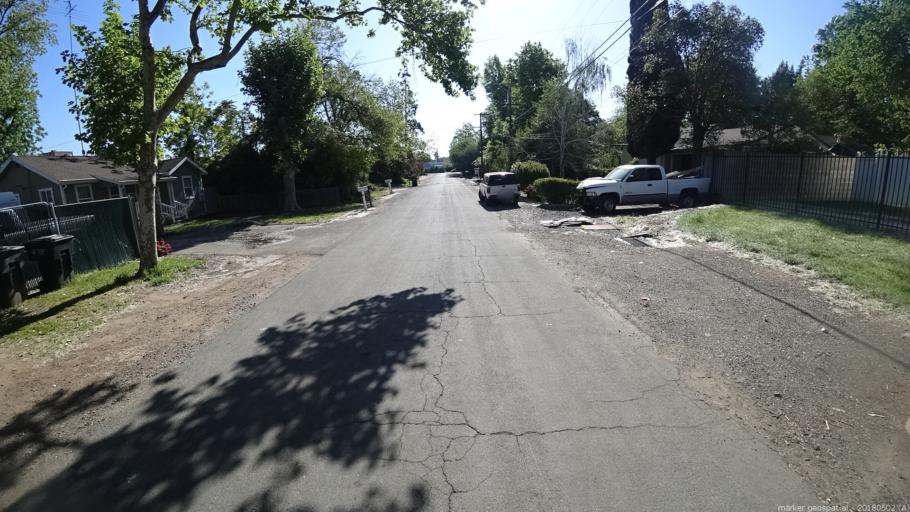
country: US
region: California
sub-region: Sacramento County
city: Arden-Arcade
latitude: 38.6202
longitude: -121.4223
